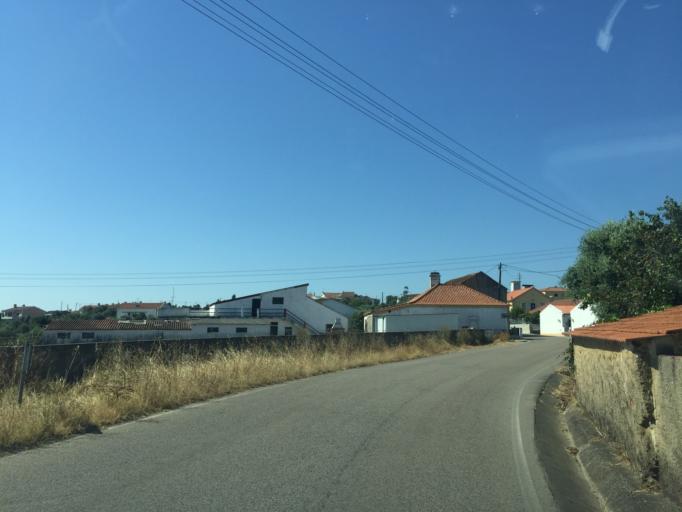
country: PT
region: Santarem
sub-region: Tomar
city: Tomar
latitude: 39.5861
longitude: -8.3272
